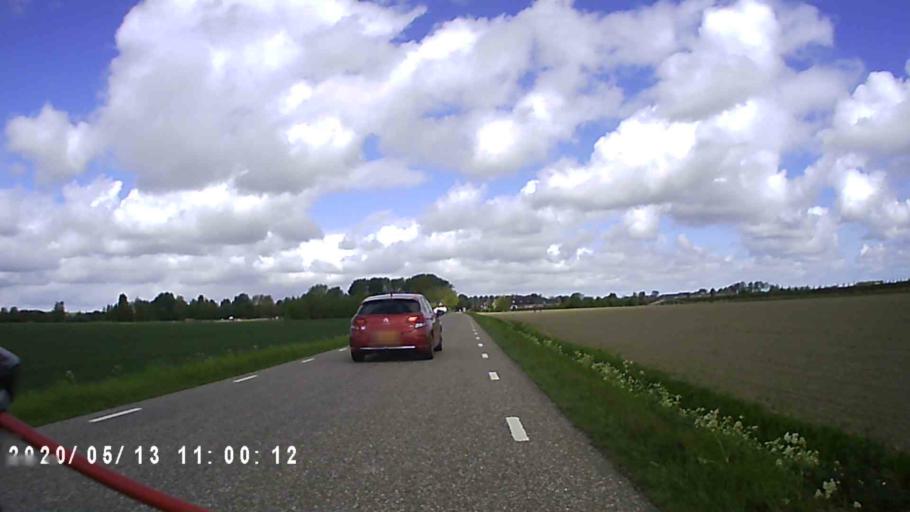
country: NL
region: Groningen
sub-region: Gemeente Zuidhorn
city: Grijpskerk
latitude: 53.2789
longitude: 6.3304
